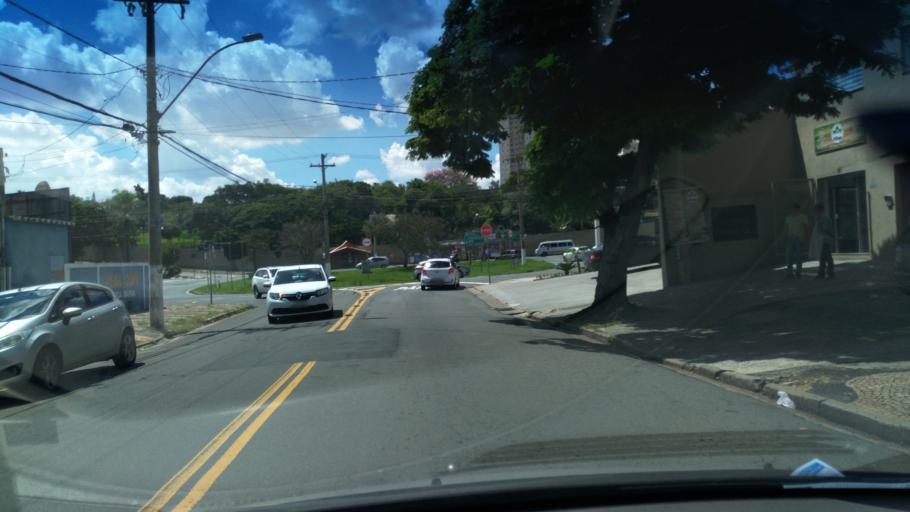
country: BR
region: Sao Paulo
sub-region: Campinas
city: Campinas
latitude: -22.9314
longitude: -47.0377
